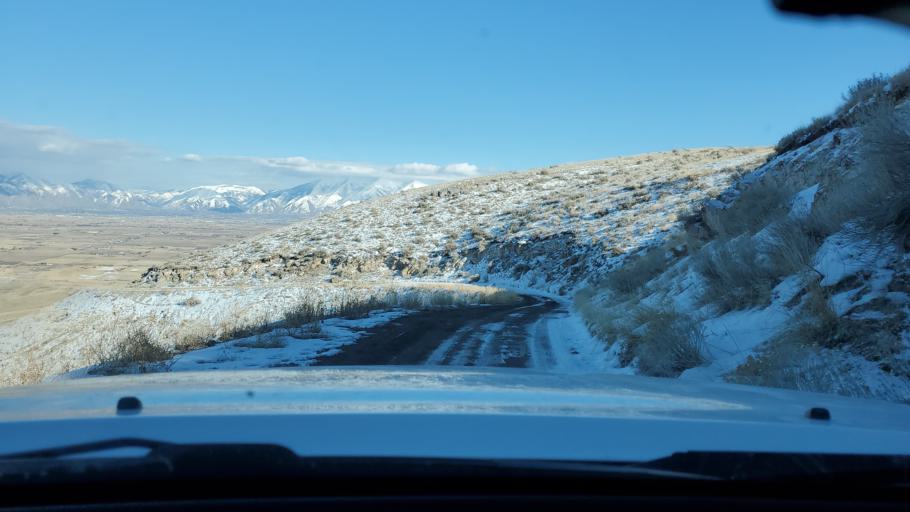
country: US
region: Utah
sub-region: Utah County
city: West Mountain
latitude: 40.1167
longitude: -111.8252
